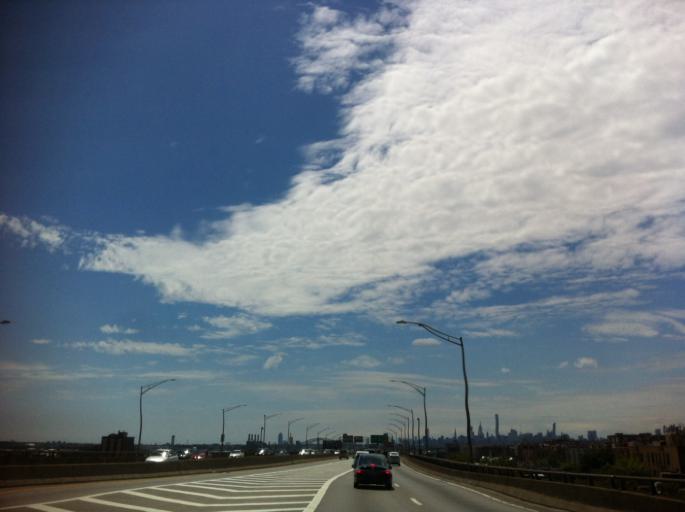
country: US
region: New York
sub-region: Bronx
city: The Bronx
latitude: 40.8197
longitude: -73.8913
